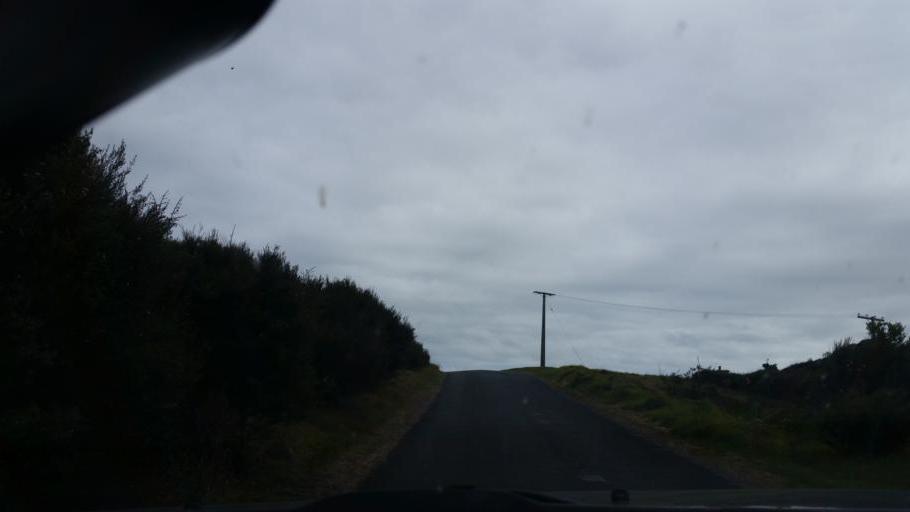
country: NZ
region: Northland
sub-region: Kaipara District
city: Dargaville
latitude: -35.8130
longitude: 173.6446
